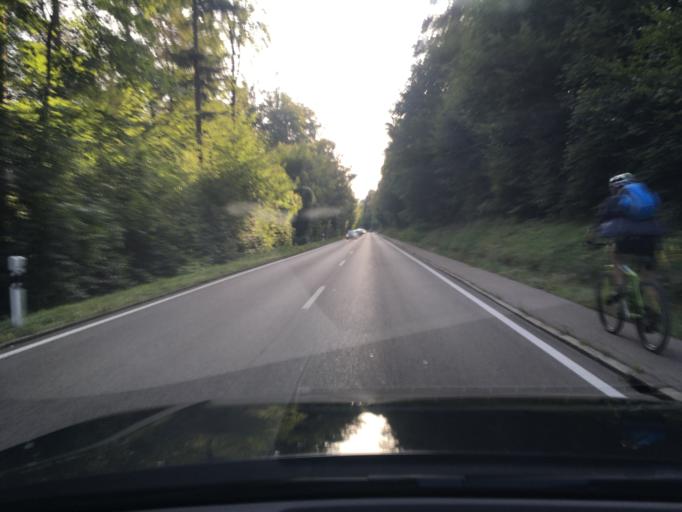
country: DE
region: Baden-Wuerttemberg
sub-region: Regierungsbezirk Stuttgart
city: Urbach
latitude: 48.7912
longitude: 9.5613
